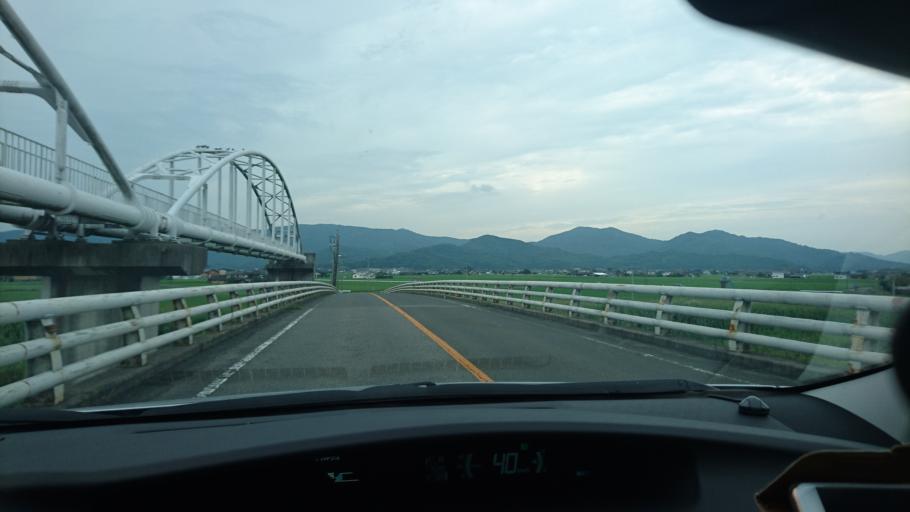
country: JP
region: Saga Prefecture
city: Takeocho-takeo
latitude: 33.2000
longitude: 130.1170
